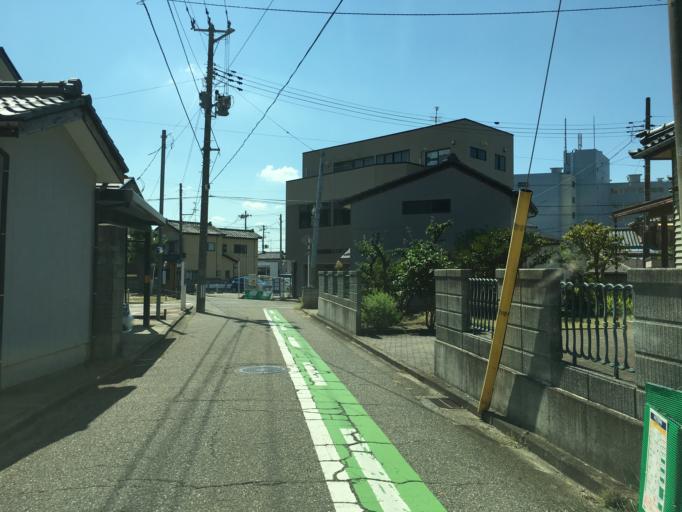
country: JP
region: Niigata
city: Niigata-shi
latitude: 37.9024
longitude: 139.0142
